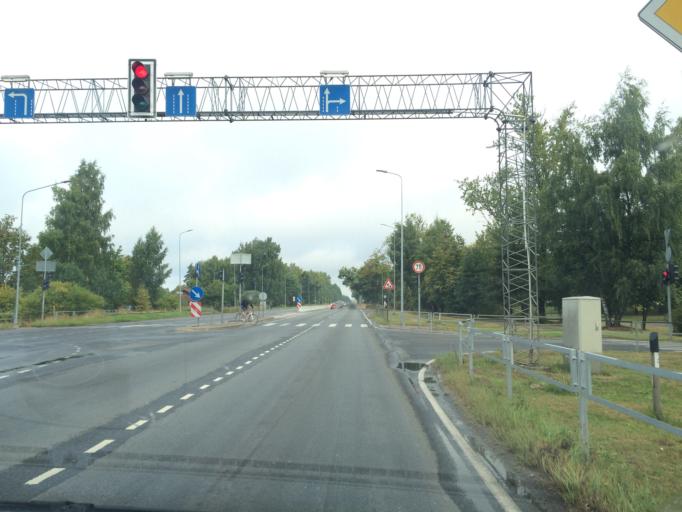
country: LV
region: Kekava
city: Kekava
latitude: 56.8701
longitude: 24.2746
